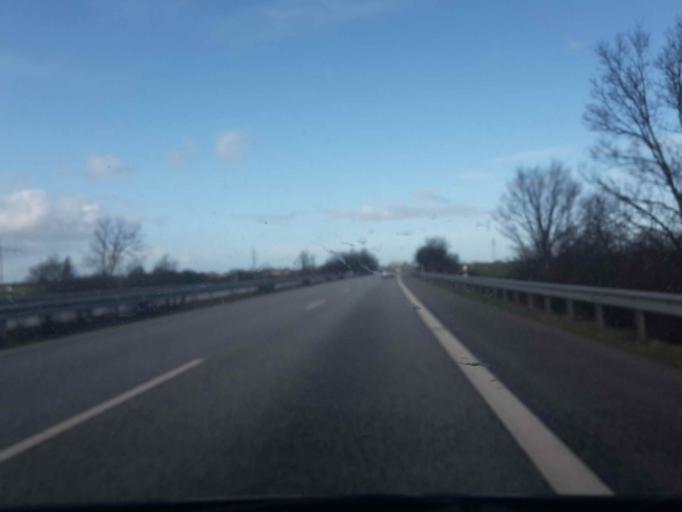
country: DE
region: Schleswig-Holstein
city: Damlos
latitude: 54.2469
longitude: 10.8887
